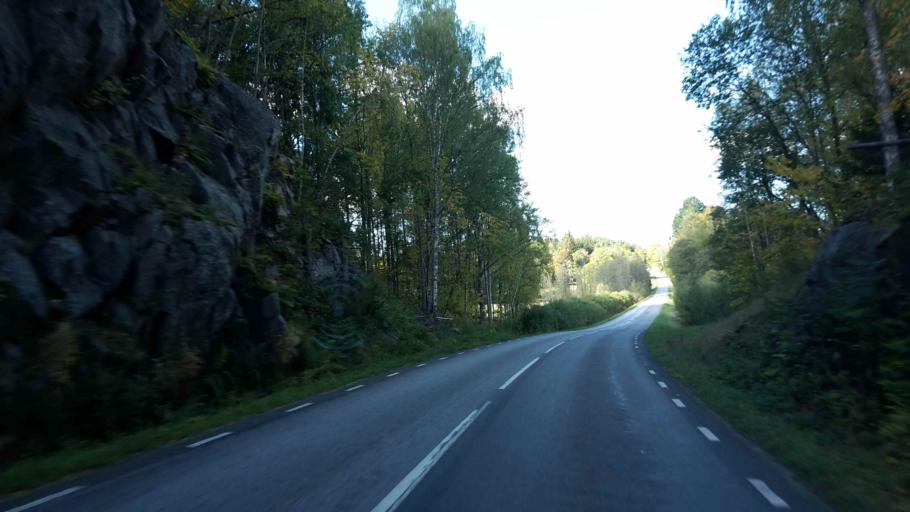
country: SE
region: OEstergoetland
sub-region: Atvidabergs Kommun
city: Atvidaberg
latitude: 58.1588
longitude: 16.1527
